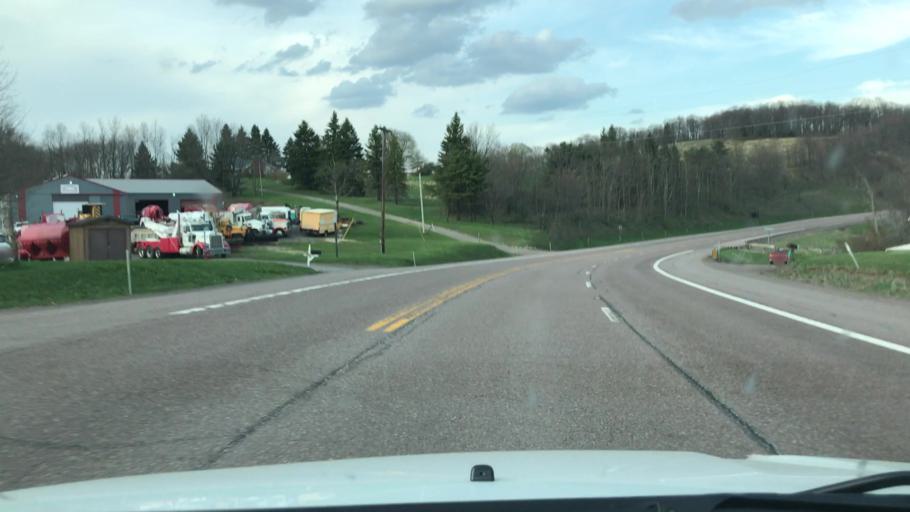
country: US
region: Pennsylvania
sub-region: Somerset County
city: Meyersdale
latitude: 39.6795
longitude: -79.2861
